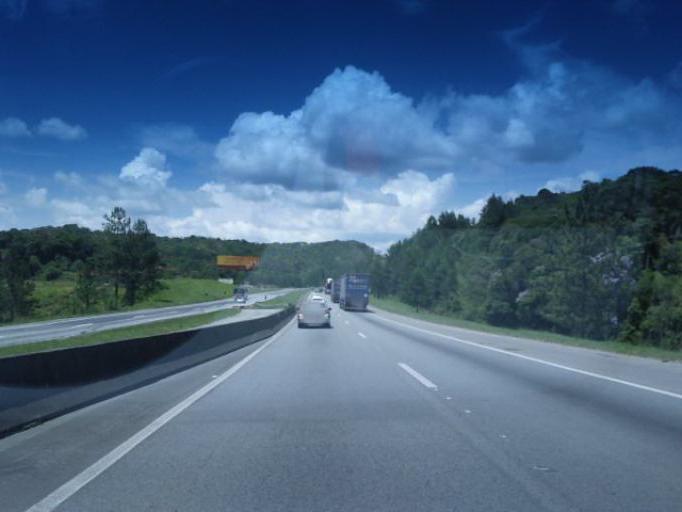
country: BR
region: Sao Paulo
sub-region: Juquitiba
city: Juquitiba
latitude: -23.9529
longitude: -47.1050
